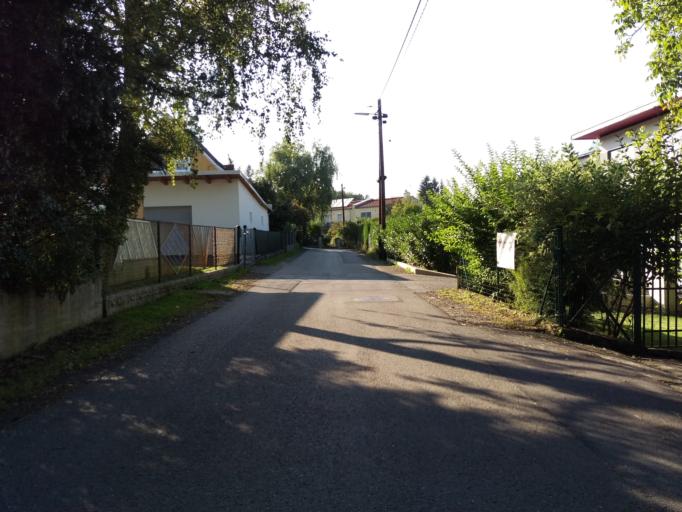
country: AT
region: Styria
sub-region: Graz Stadt
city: Mariatrost
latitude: 47.0735
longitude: 15.5006
